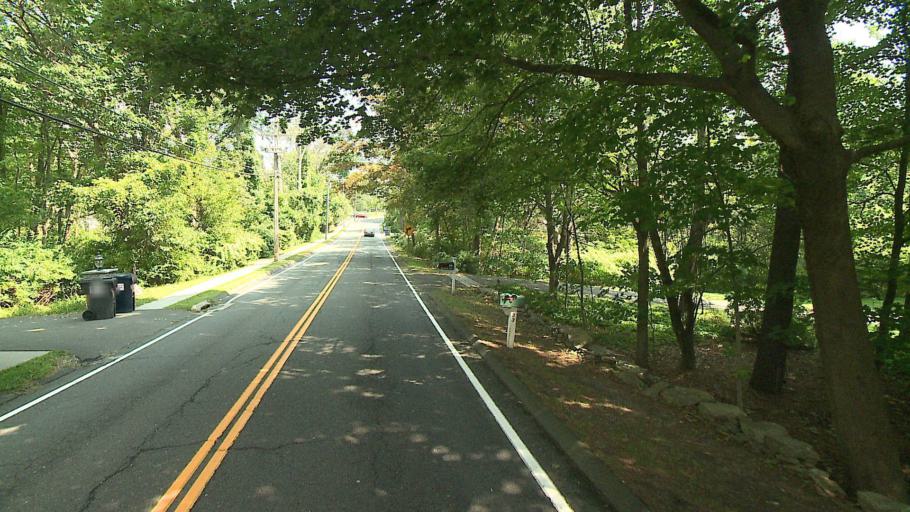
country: US
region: Connecticut
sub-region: Fairfield County
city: Ridgefield
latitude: 41.2759
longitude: -73.4945
